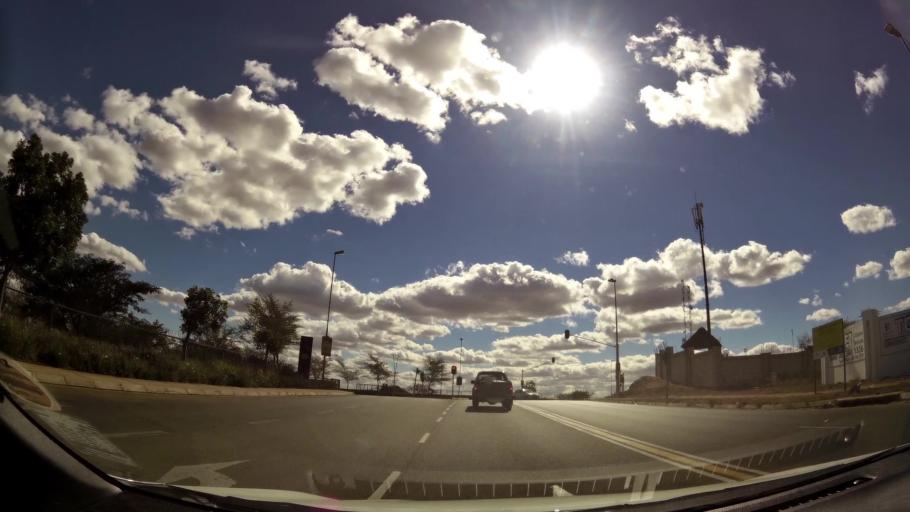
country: ZA
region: Limpopo
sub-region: Capricorn District Municipality
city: Polokwane
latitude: -23.8707
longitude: 29.5095
